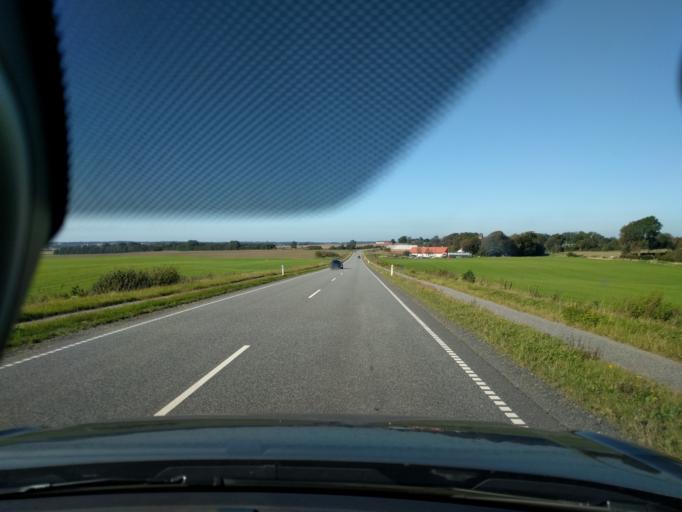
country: DK
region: North Denmark
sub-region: Vesthimmerland Kommune
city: Aars
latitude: 56.7423
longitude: 9.5957
